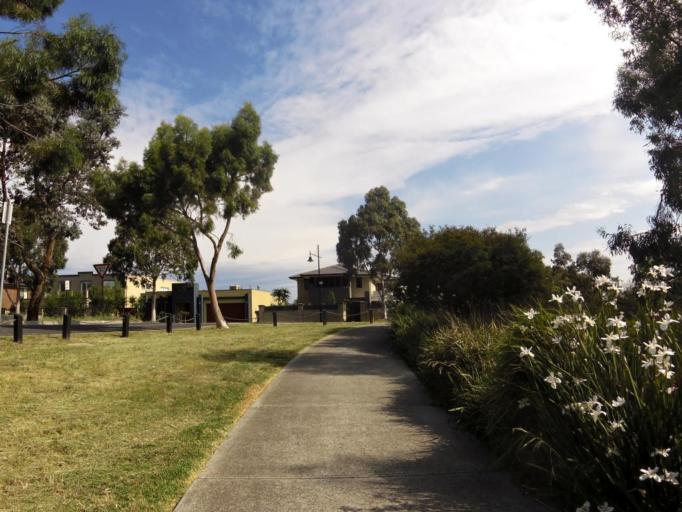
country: AU
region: Victoria
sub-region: Whittlesea
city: Epping
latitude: -37.6292
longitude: 145.0340
